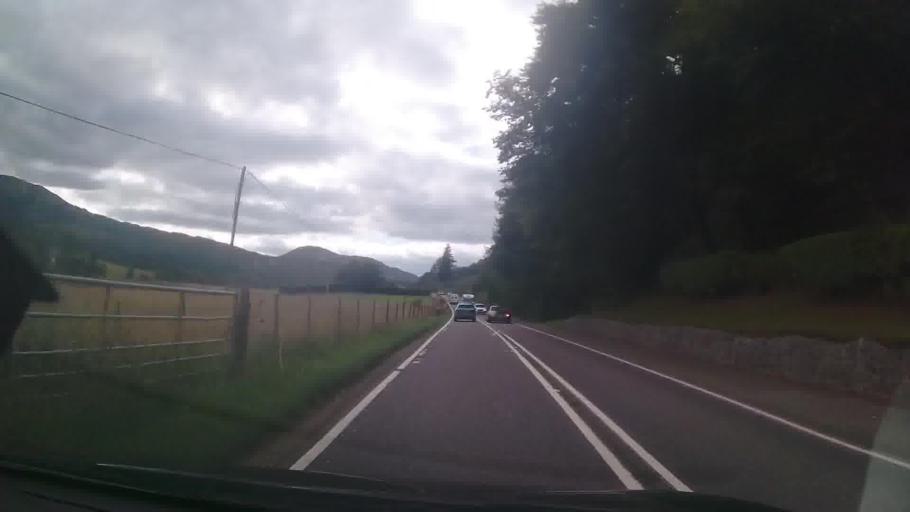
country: GB
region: Scotland
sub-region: Highland
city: Fort William
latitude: 56.6539
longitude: -5.2641
